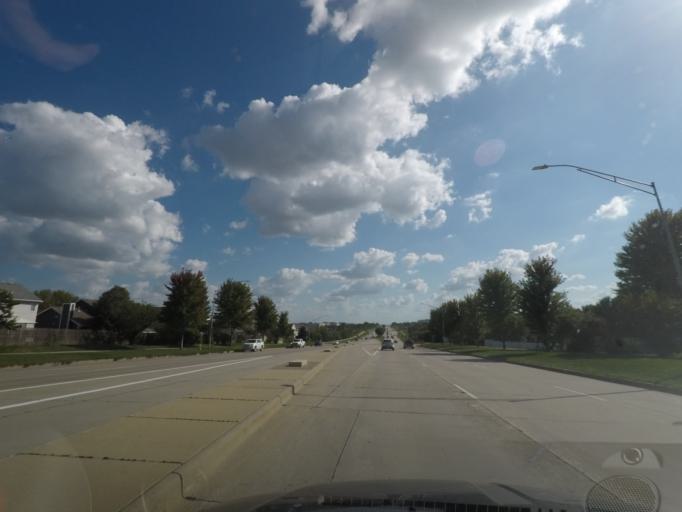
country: US
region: Iowa
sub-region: Dallas County
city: Waukee
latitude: 41.5780
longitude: -93.8093
